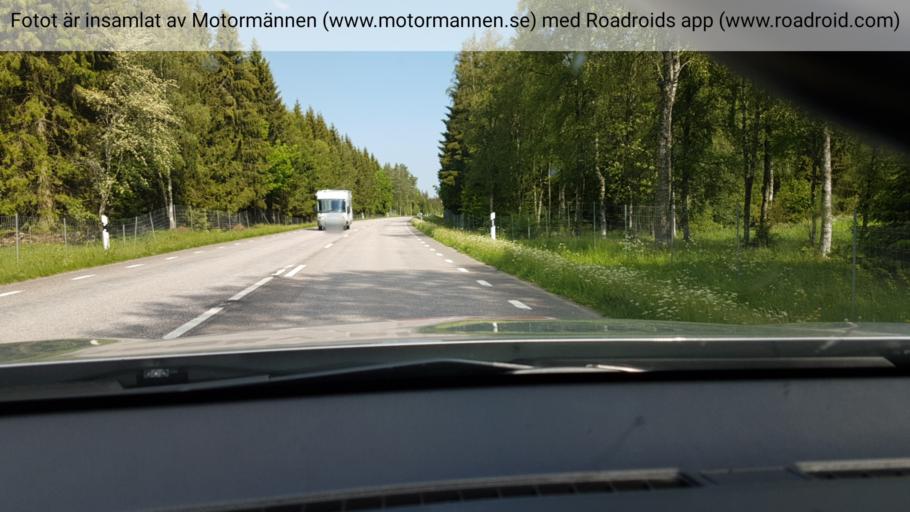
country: SE
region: Vaestra Goetaland
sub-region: Falkopings Kommun
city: Falkoeping
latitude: 58.0320
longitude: 13.5478
